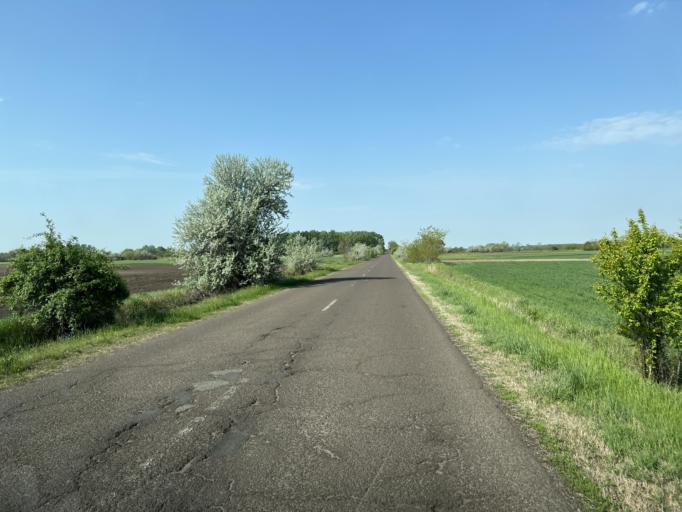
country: HU
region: Pest
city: Jaszkarajeno
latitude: 47.0377
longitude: 20.0458
